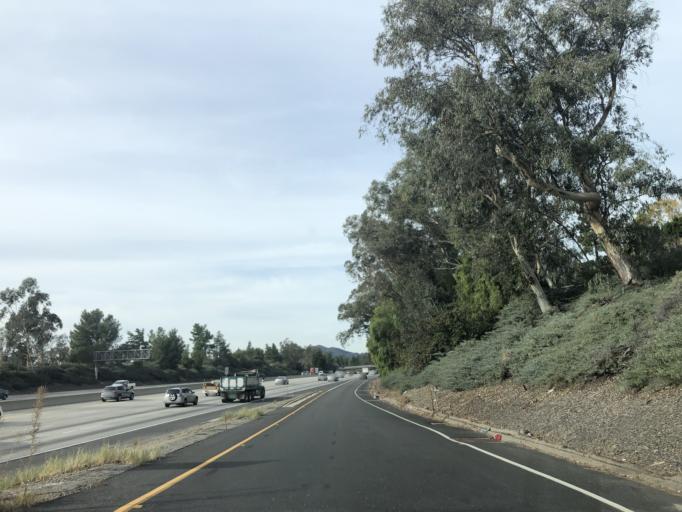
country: US
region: California
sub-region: Los Angeles County
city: Northridge
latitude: 34.2748
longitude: -118.5403
